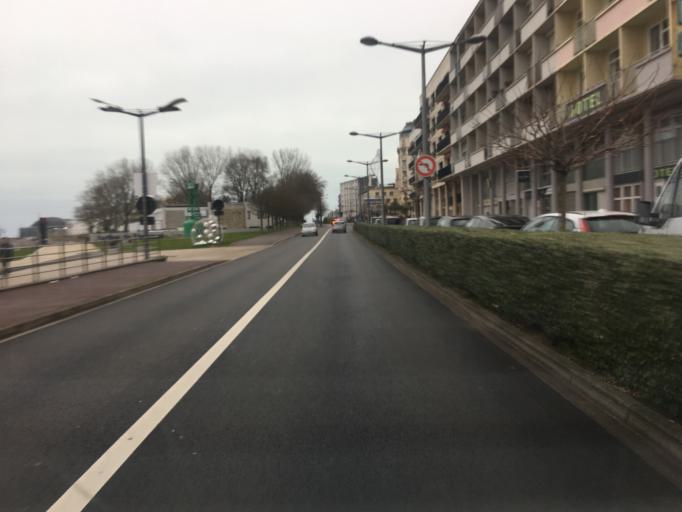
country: FR
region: Nord-Pas-de-Calais
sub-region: Departement du Pas-de-Calais
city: Saint-Martin-Boulogne
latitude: 50.7278
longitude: 1.5988
